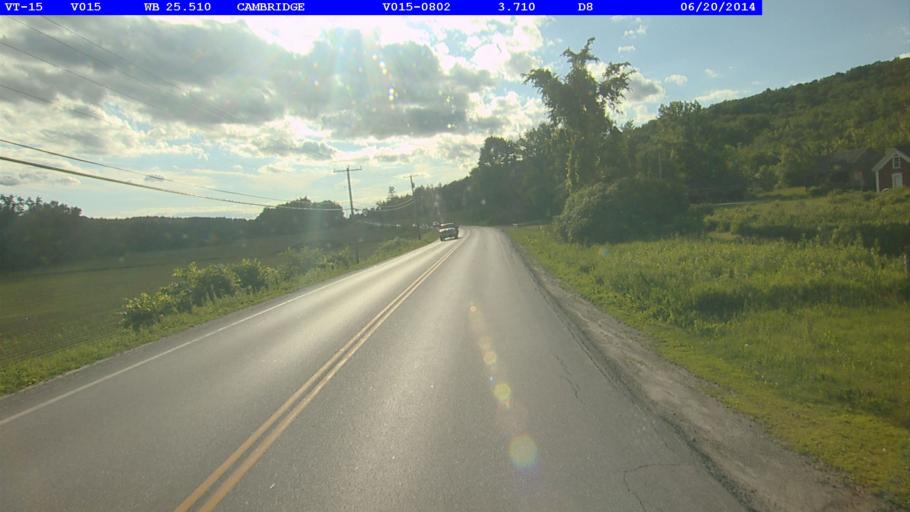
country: US
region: Vermont
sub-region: Lamoille County
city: Johnson
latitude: 44.6451
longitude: -72.8556
